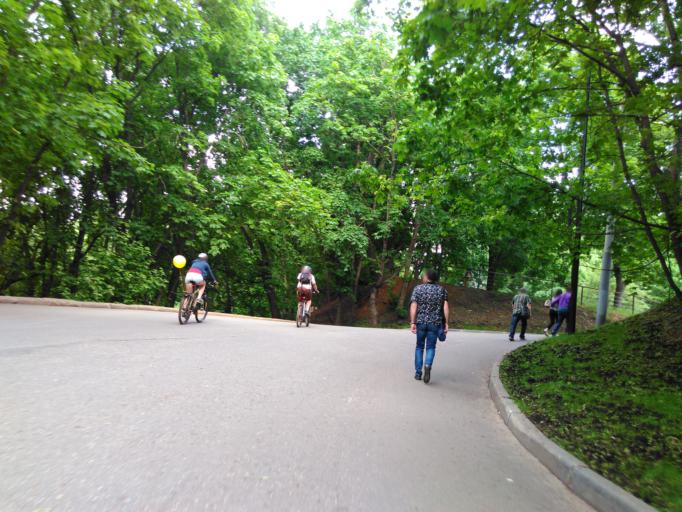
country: RU
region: Moscow
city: Luzhniki
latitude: 55.7076
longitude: 37.5596
